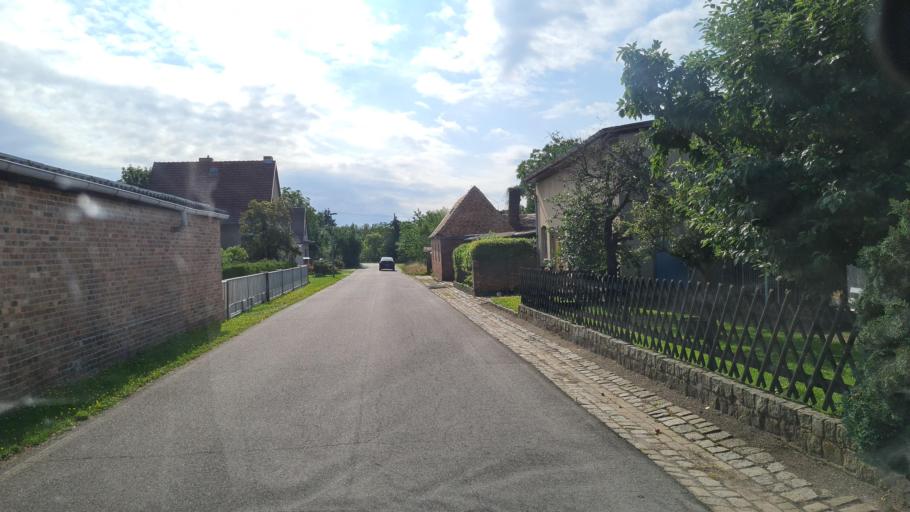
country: DE
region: Brandenburg
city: Grossraschen
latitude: 51.5498
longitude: 14.0614
